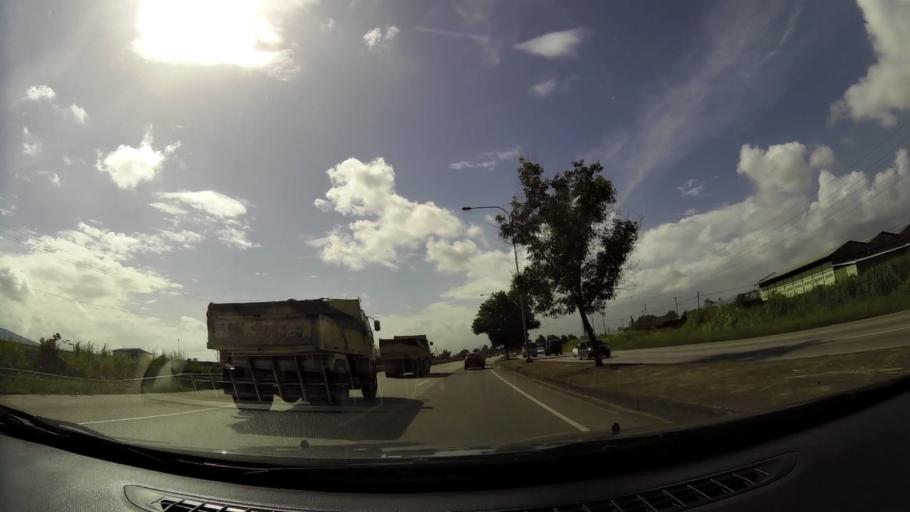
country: TT
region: Borough of Arima
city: Arima
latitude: 10.6068
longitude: -61.2809
